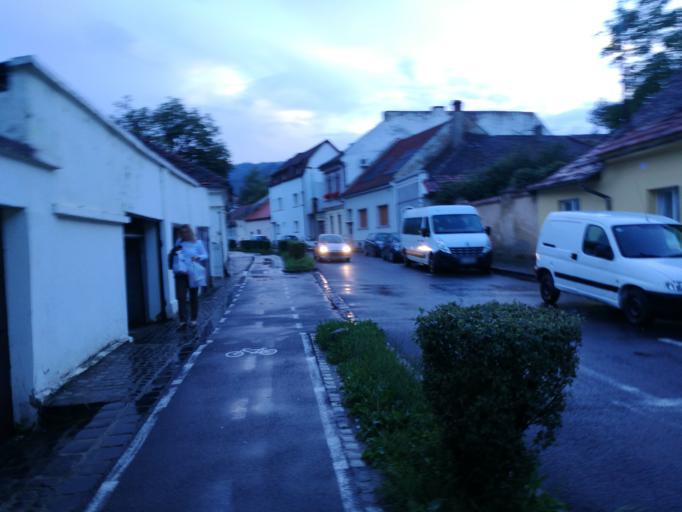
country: RO
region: Brasov
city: Brasov
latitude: 45.6385
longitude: 25.5832
